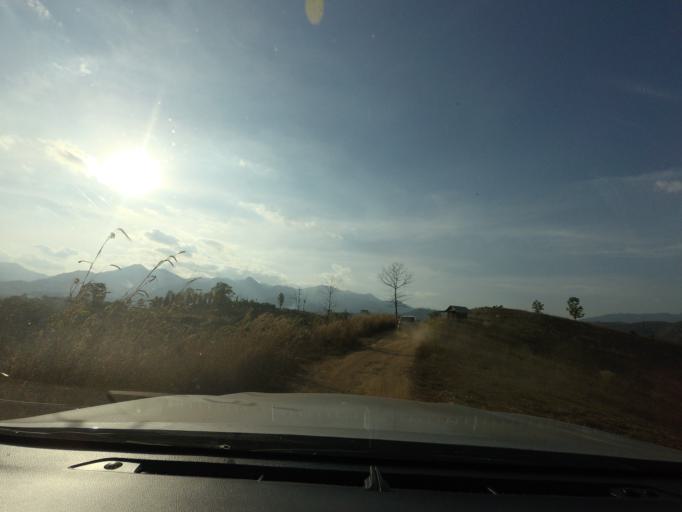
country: TH
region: Mae Hong Son
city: Wiang Nuea
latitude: 19.4007
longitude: 98.4083
